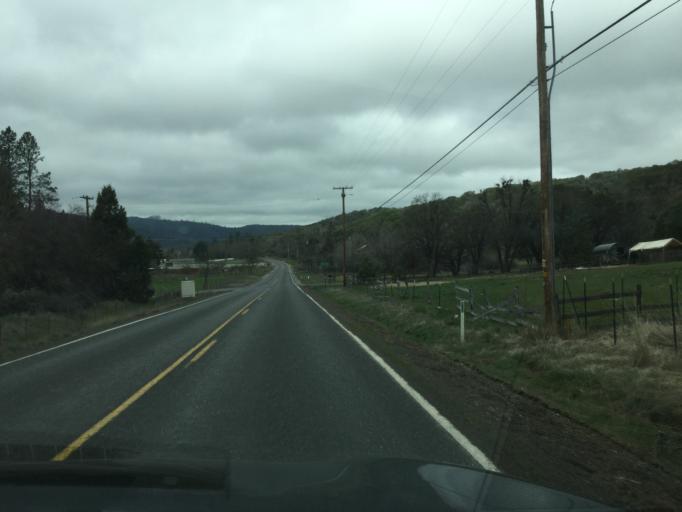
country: US
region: Oregon
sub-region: Jackson County
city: Gold Hill
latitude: 42.3932
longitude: -122.9955
